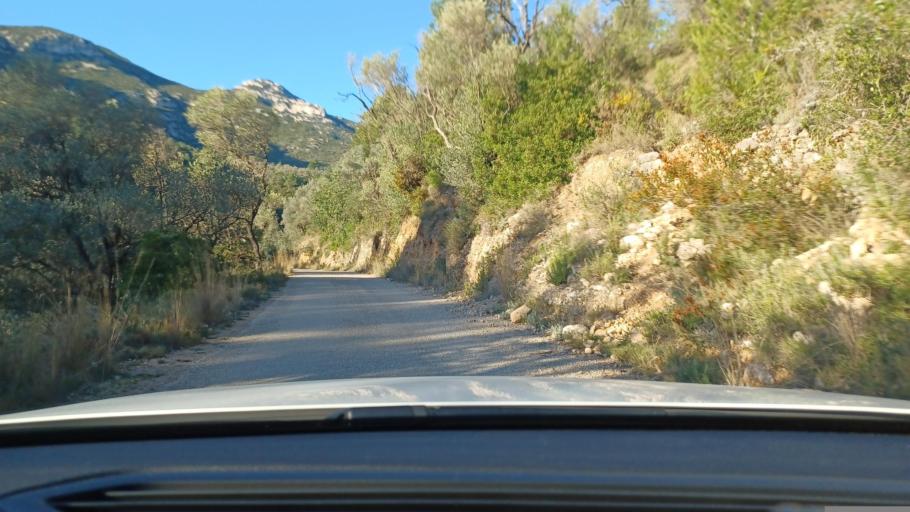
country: ES
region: Catalonia
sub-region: Provincia de Tarragona
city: Mas de Barberans
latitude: 40.7218
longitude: 0.3445
